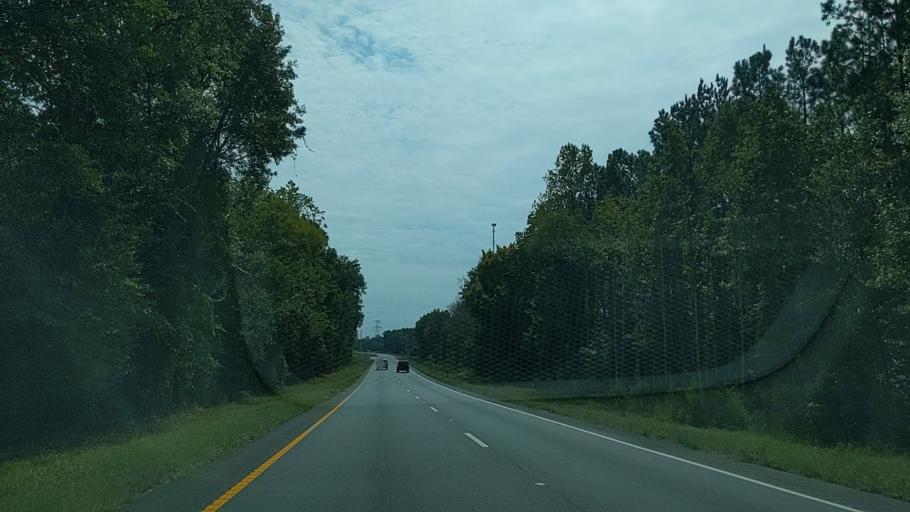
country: US
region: Georgia
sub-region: Effingham County
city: Rincon
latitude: 32.2471
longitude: -81.2087
